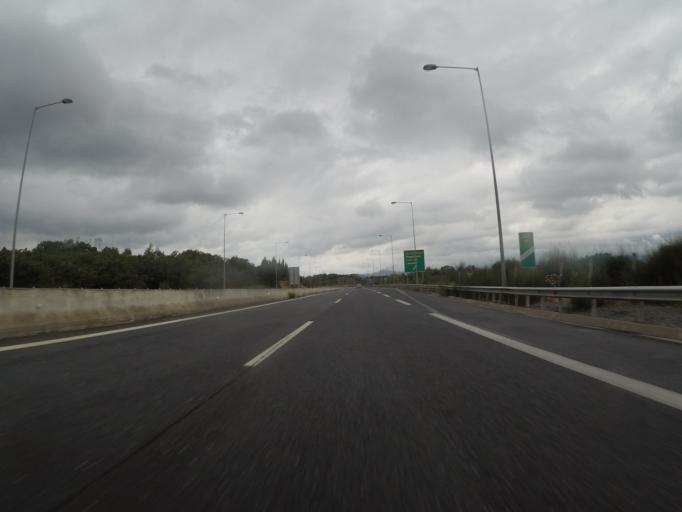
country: GR
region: Peloponnese
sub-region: Nomos Arkadias
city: Megalopoli
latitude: 37.3588
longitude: 22.1368
